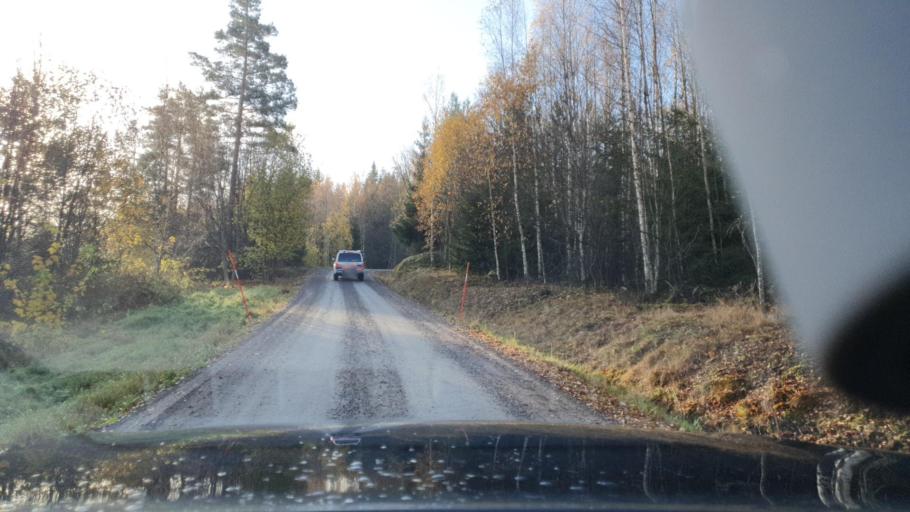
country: SE
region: Vaermland
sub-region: Grums Kommun
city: Grums
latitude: 59.4764
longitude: 12.9286
